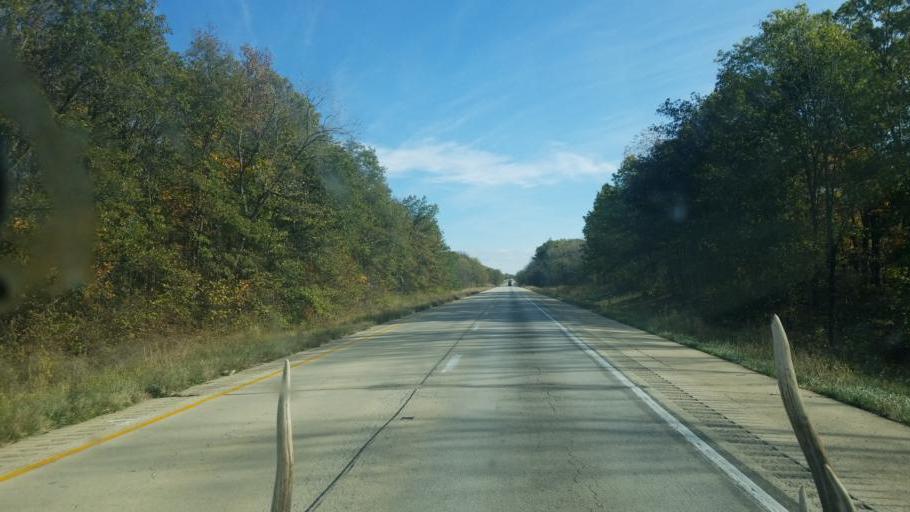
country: US
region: Illinois
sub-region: Effingham County
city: Effingham
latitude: 39.0772
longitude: -88.6391
